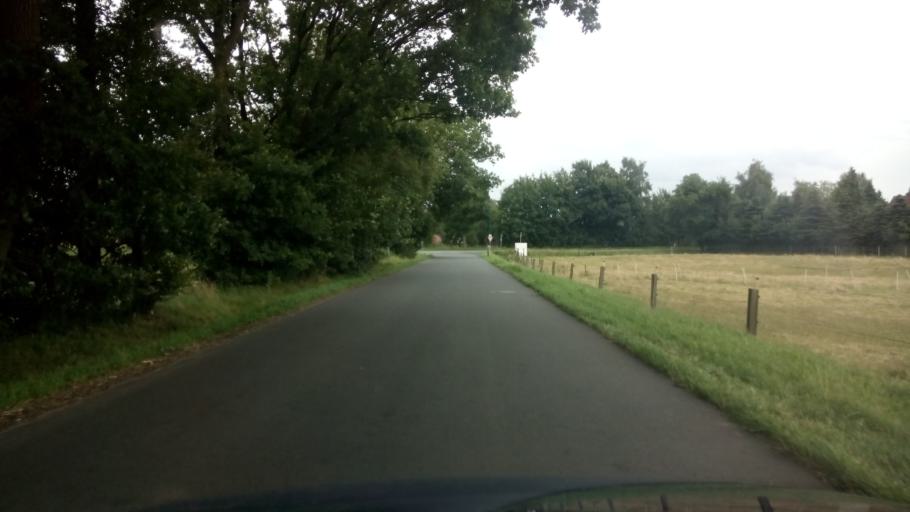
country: DE
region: Lower Saxony
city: Hambergen
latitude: 53.2985
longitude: 8.8342
